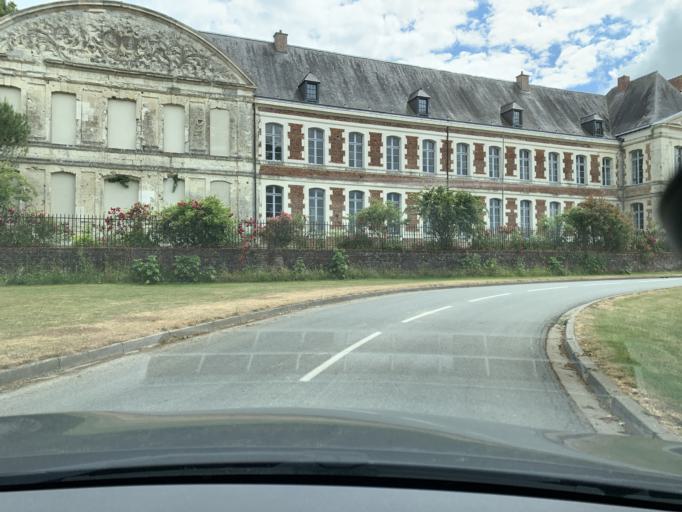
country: FR
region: Nord-Pas-de-Calais
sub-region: Departement du Nord
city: Masnieres
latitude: 50.0776
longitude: 3.2231
